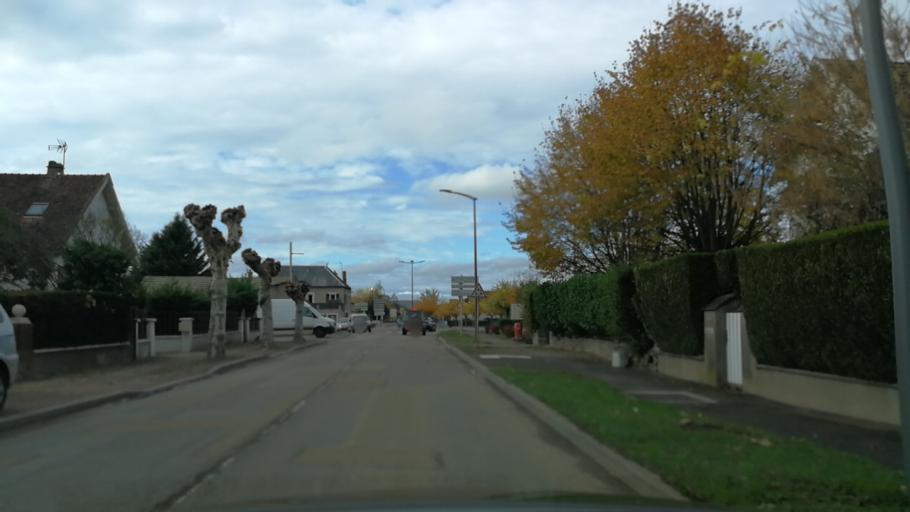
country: FR
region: Bourgogne
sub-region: Departement de la Cote-d'Or
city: Pouilly-en-Auxois
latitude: 47.2684
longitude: 4.5476
